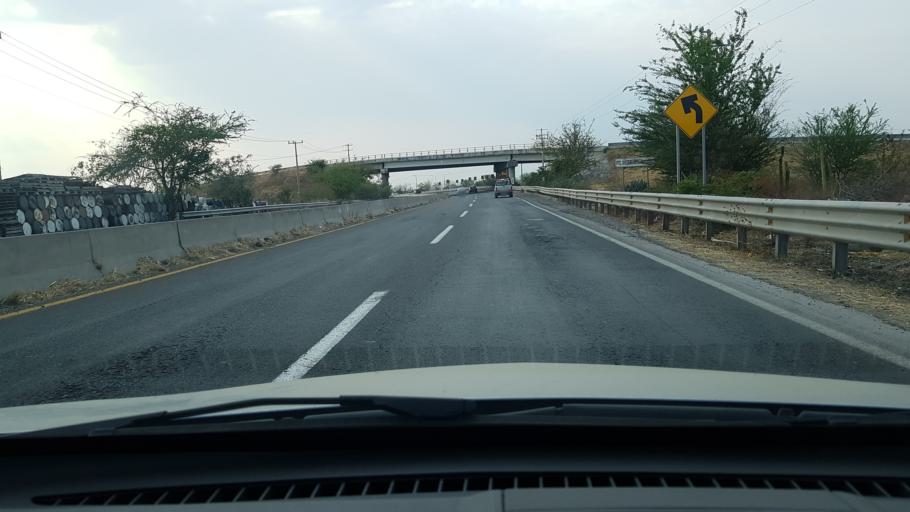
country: MX
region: Morelos
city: Amayuca
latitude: 18.7296
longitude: -98.8107
